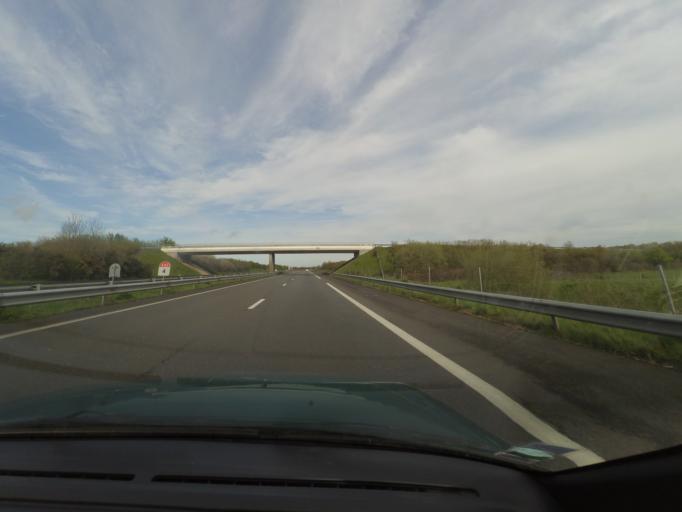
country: FR
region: Pays de la Loire
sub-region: Departement de la Loire-Atlantique
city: Le Bignon
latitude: 47.1034
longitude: -1.4781
